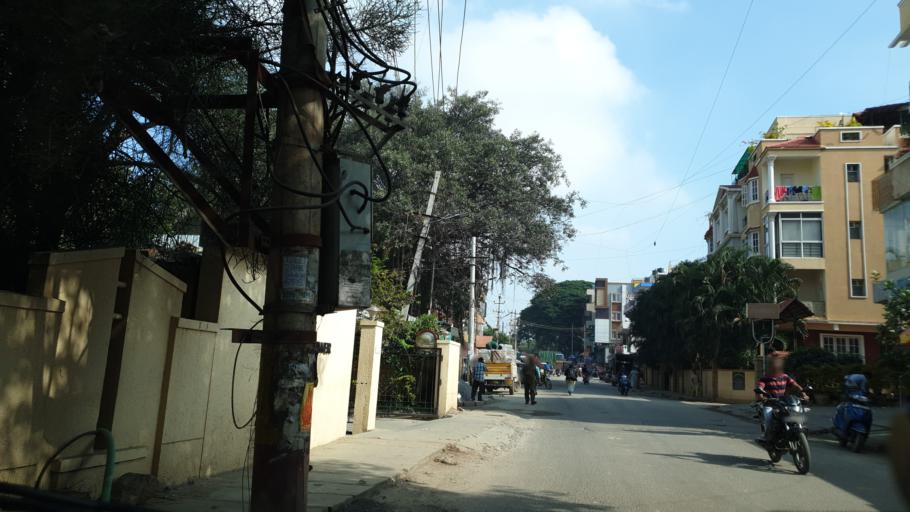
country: IN
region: Karnataka
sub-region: Bangalore Urban
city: Bangalore
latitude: 12.9678
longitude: 77.6826
